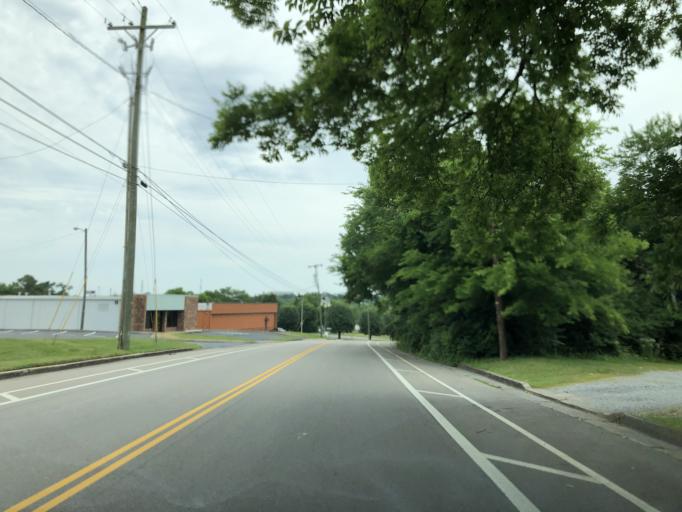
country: US
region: Tennessee
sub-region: Davidson County
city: Goodlettsville
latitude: 36.2947
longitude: -86.7052
